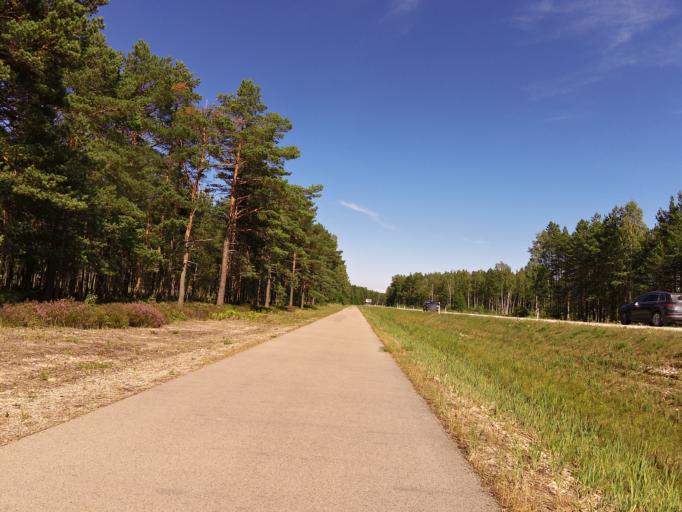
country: EE
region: Hiiumaa
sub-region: Kaerdla linn
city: Kardla
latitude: 59.0088
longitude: 22.6258
